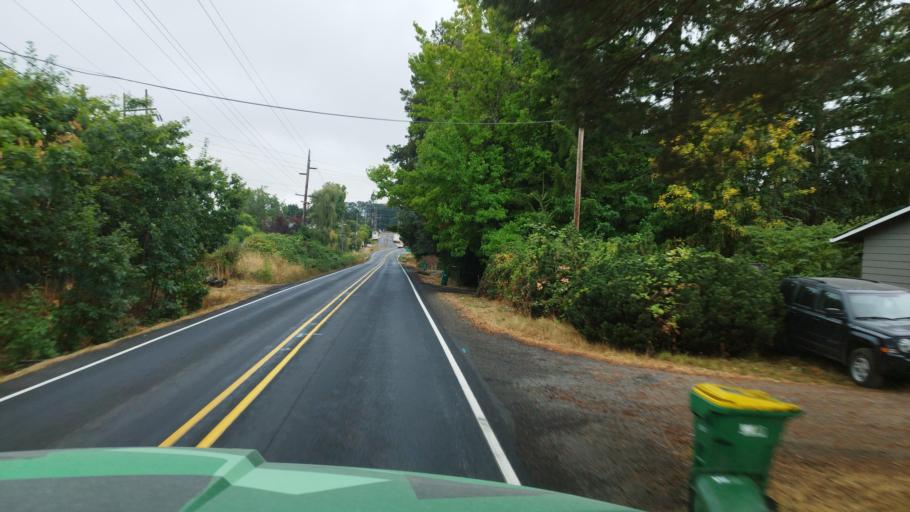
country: US
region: Oregon
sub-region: Washington County
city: Cornelius
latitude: 45.5290
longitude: -123.0822
